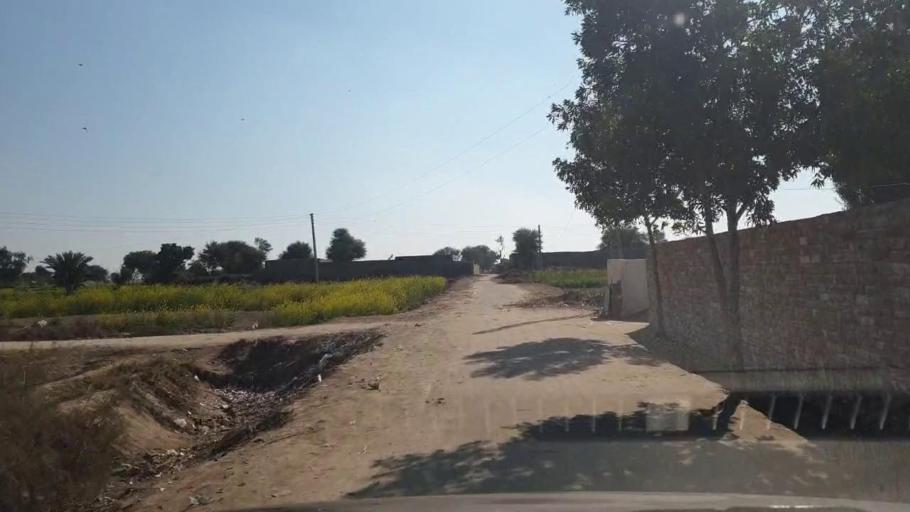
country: PK
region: Sindh
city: Shahpur Chakar
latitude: 26.1067
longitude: 68.6630
